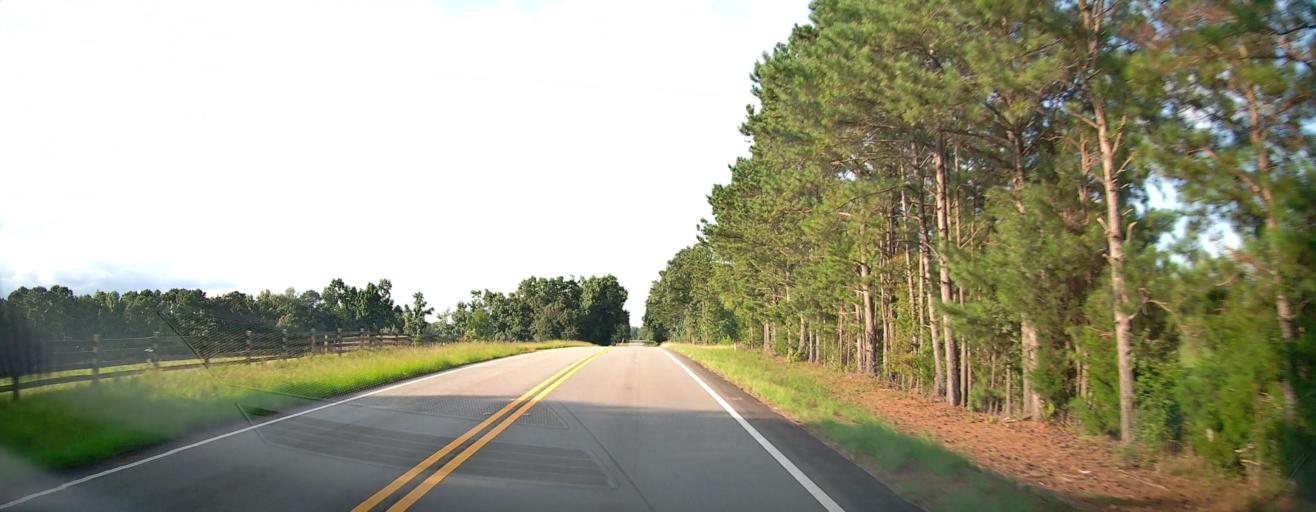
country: US
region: Georgia
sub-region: Monroe County
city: Forsyth
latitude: 32.8926
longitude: -83.9940
